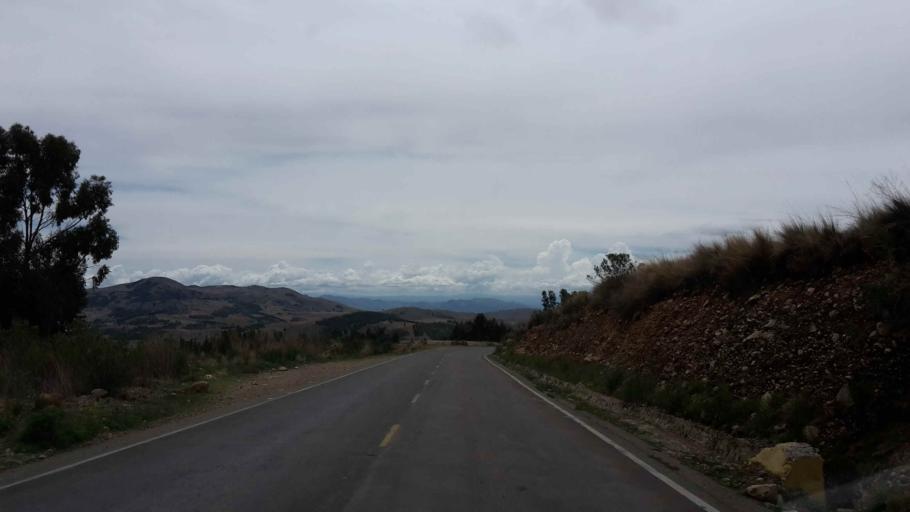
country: BO
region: Cochabamba
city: Arani
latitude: -17.4618
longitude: -65.6804
